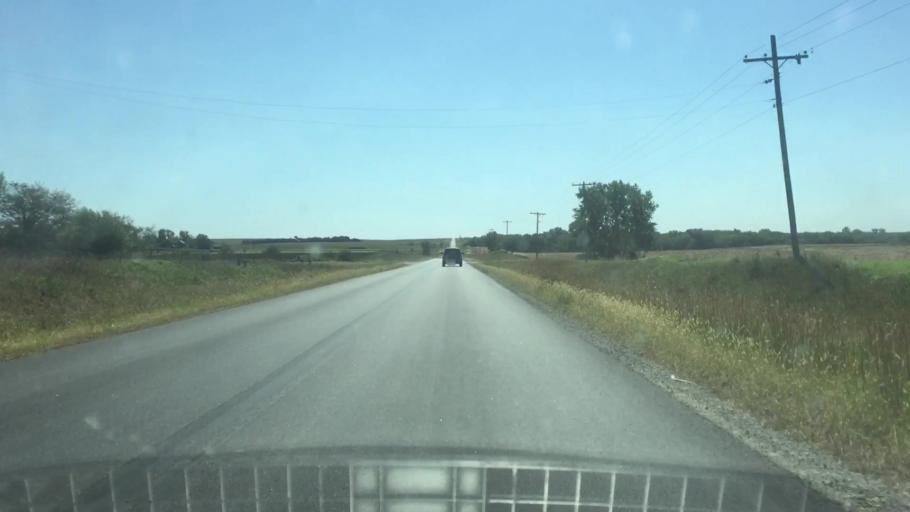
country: US
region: Kansas
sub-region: Marshall County
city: Marysville
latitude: 39.8865
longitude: -96.6009
